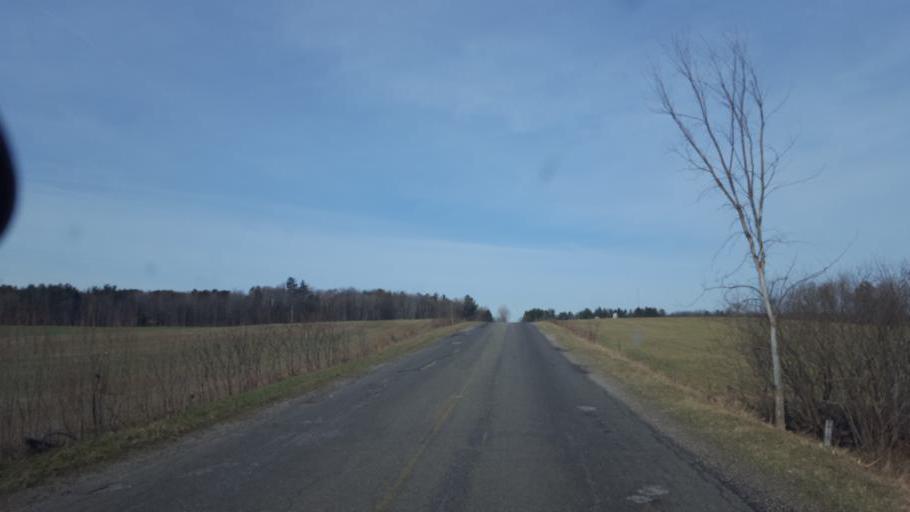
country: US
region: Michigan
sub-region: Montcalm County
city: Howard City
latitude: 43.5260
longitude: -85.4727
